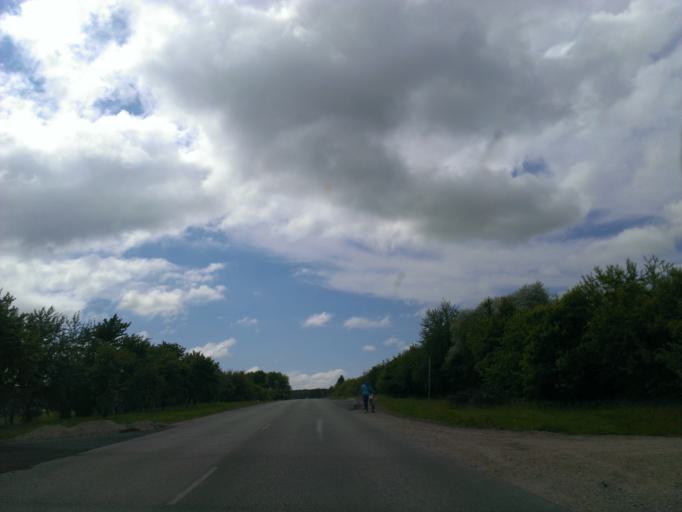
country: LV
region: Durbe
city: Liegi
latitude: 56.5827
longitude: 21.3361
